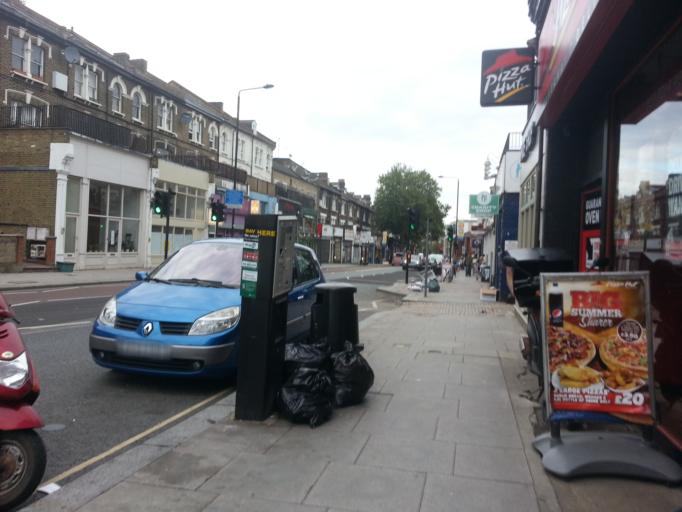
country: GB
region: England
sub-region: Greater London
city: Holloway
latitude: 51.5556
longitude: -0.1393
